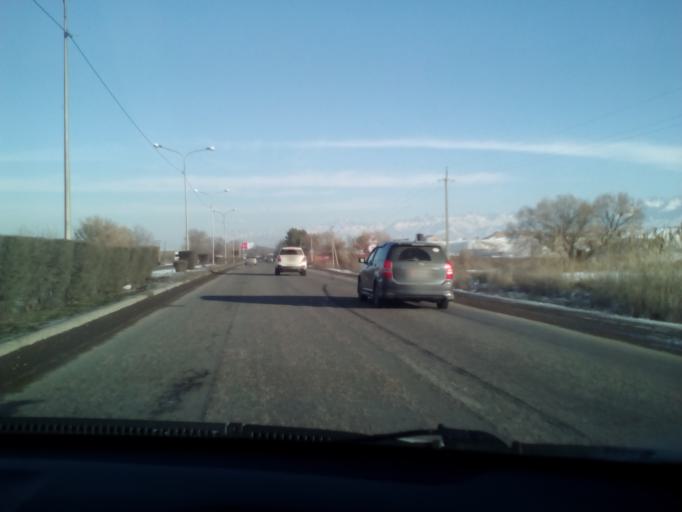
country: KZ
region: Almaty Oblysy
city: Burunday
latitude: 43.2225
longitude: 76.4233
